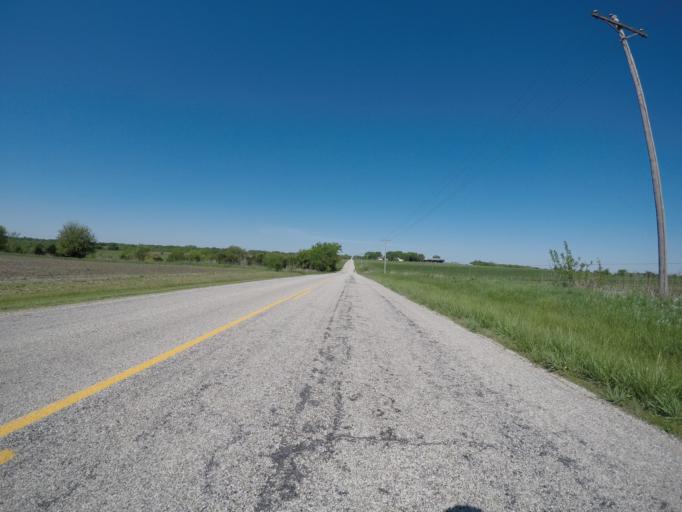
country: US
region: Kansas
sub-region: Osage County
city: Overbrook
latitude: 38.8405
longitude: -95.5113
